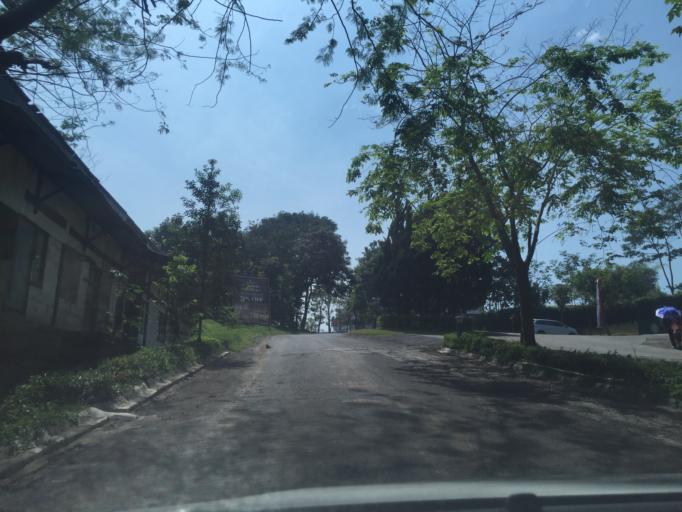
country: ID
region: West Java
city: Bandung
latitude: -6.8651
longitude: 107.6420
